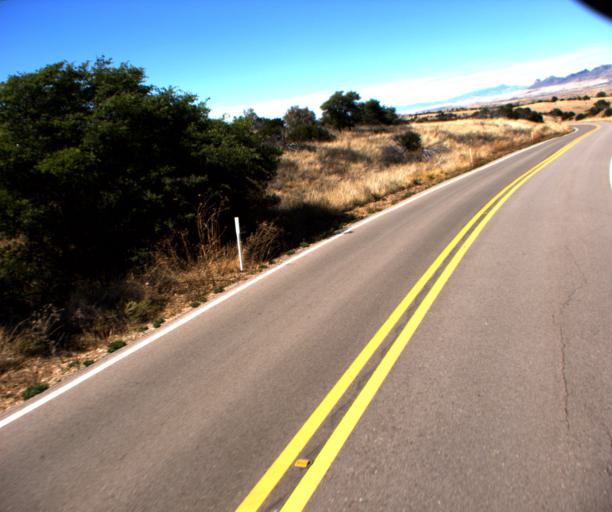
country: US
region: Arizona
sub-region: Cochise County
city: Huachuca City
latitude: 31.5202
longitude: -110.4994
